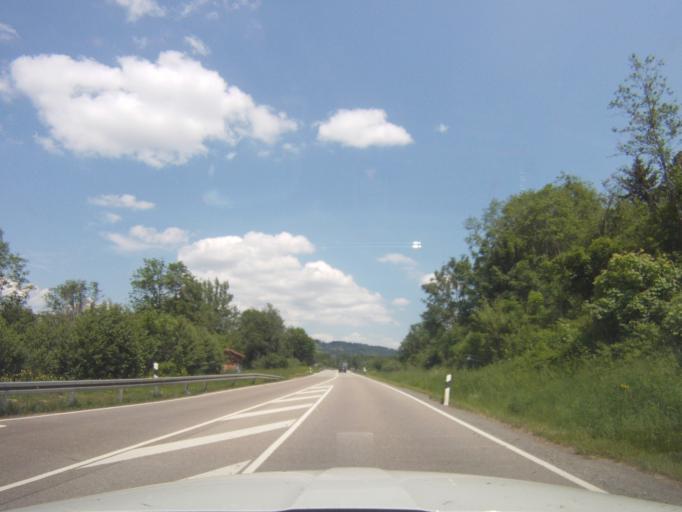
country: DE
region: Bavaria
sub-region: Swabia
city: Wertach
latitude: 47.5967
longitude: 10.4171
